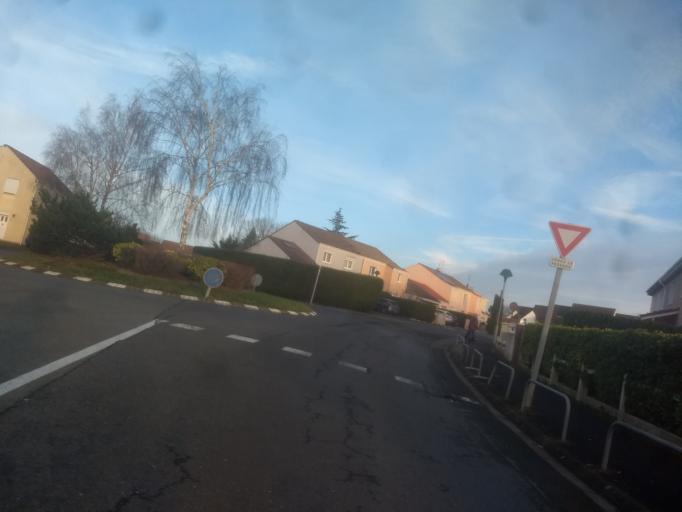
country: FR
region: Nord-Pas-de-Calais
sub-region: Departement du Pas-de-Calais
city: Agny
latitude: 50.2666
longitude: 2.7653
